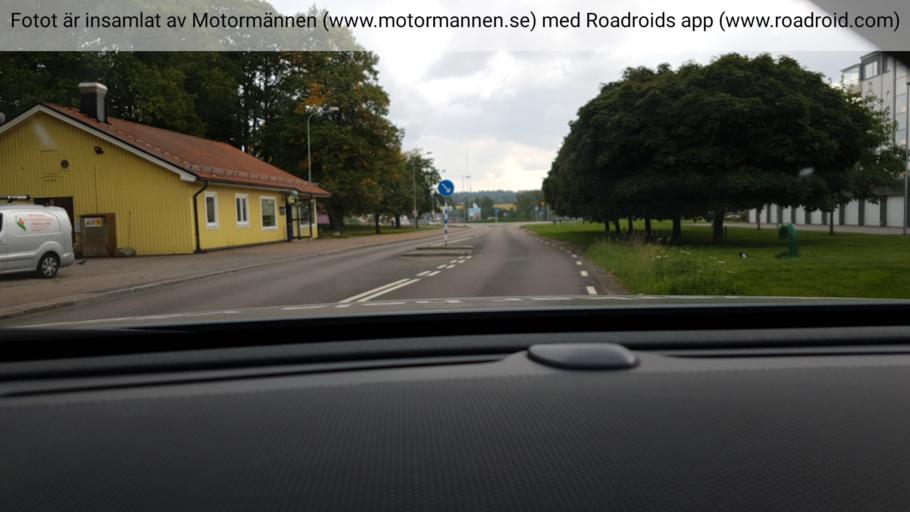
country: SE
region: Vaestra Goetaland
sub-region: Goteborg
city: Eriksbo
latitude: 57.7351
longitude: 12.0289
